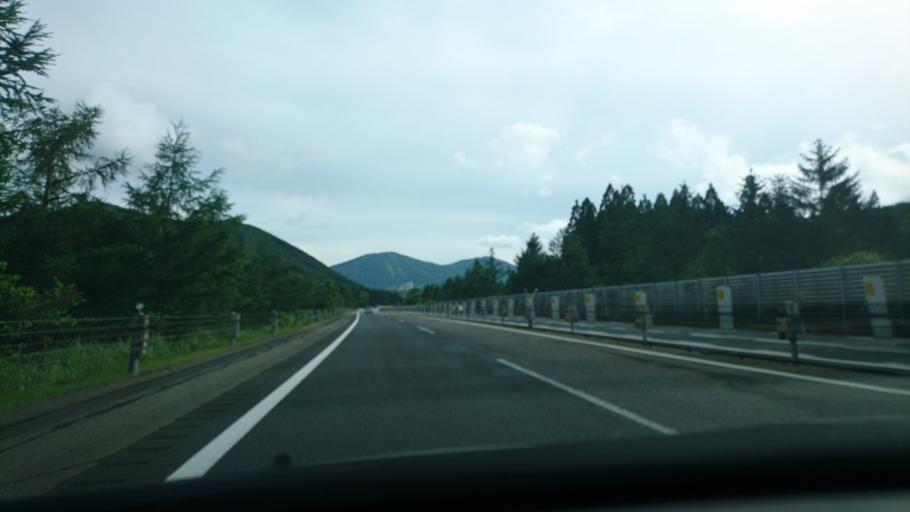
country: JP
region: Akita
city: Hanawa
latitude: 40.0398
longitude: 140.9913
